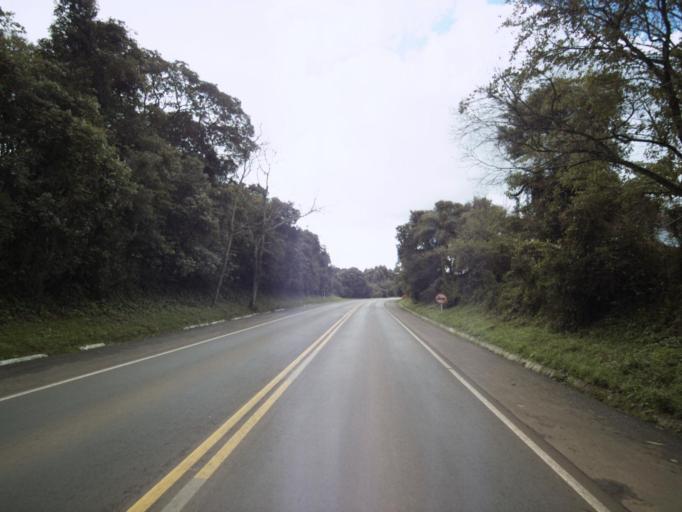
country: BR
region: Santa Catarina
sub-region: Concordia
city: Concordia
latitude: -27.2782
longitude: -51.9686
